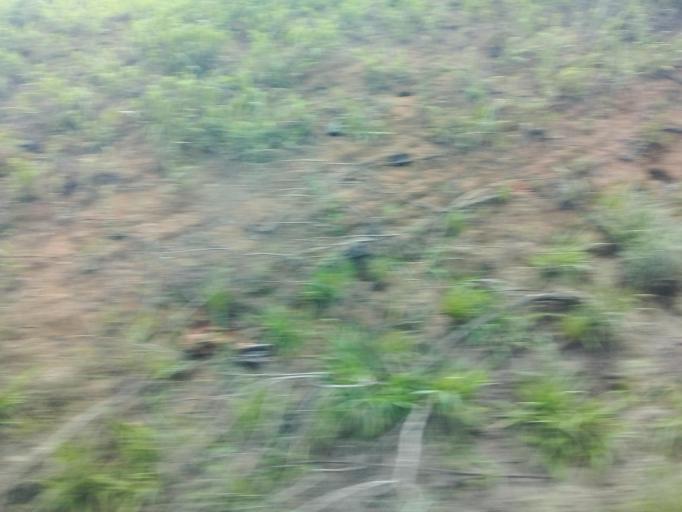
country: BR
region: Minas Gerais
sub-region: Joao Monlevade
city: Joao Monlevade
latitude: -19.8210
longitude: -43.0994
